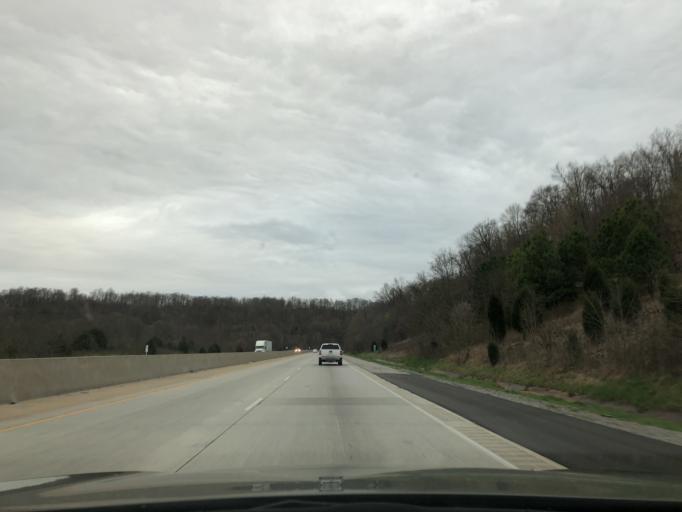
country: US
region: Arkansas
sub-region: Washington County
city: West Fork
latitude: 35.7769
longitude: -94.1864
